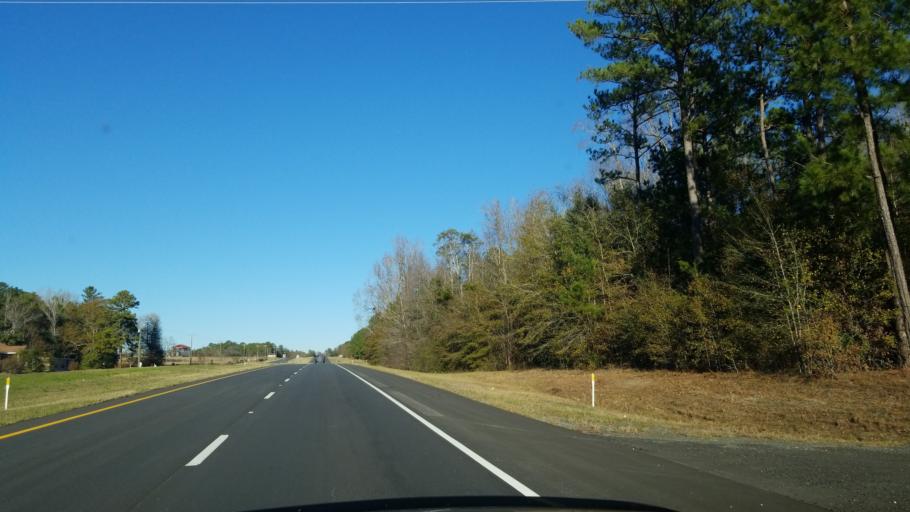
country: US
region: Georgia
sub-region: Talbot County
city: Talbotton
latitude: 32.5676
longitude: -84.6020
